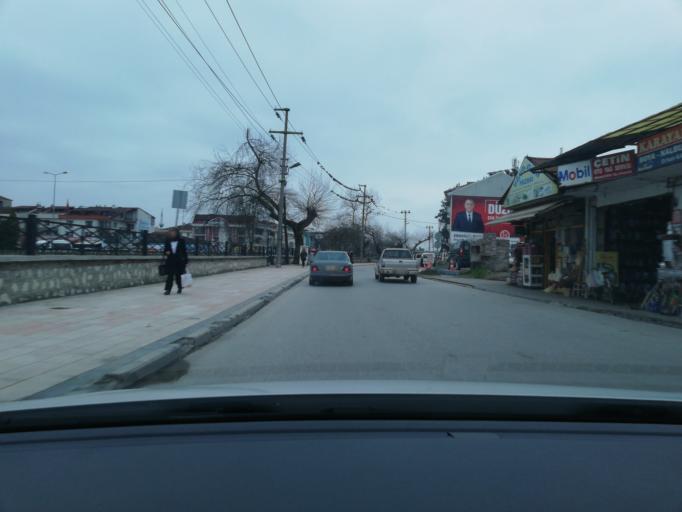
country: TR
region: Duzce
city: Duzce
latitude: 40.8363
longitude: 31.1615
